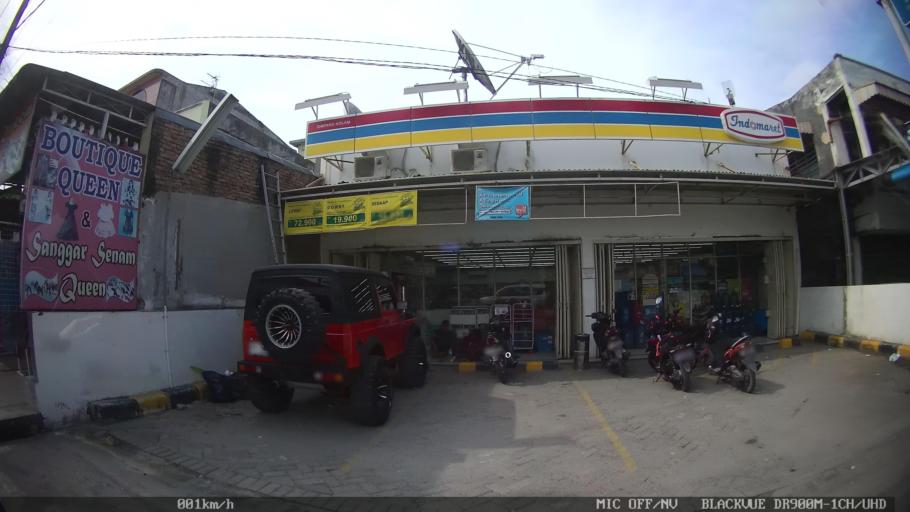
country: ID
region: North Sumatra
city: Medan
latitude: 3.6078
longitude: 98.7577
